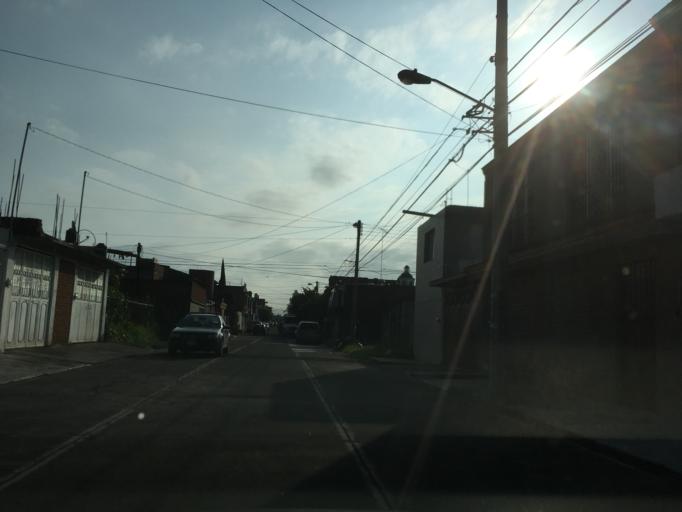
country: MX
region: Michoacan
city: Morelia
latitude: 19.6931
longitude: -101.2202
